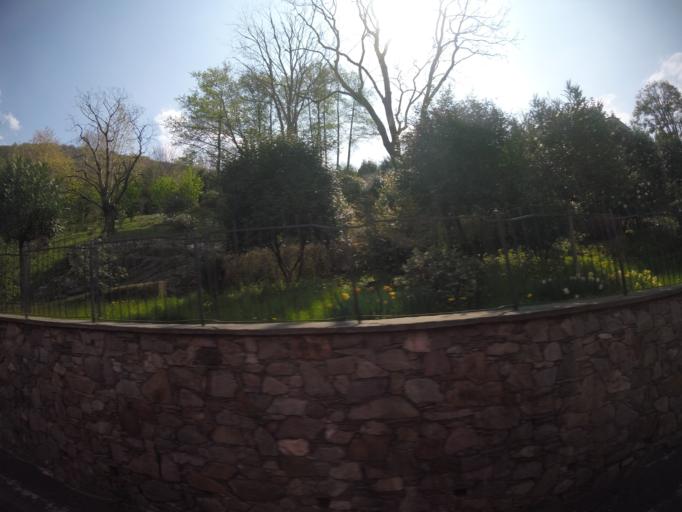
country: IT
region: Piedmont
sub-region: Provincia di Novara
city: Pettenasco
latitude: 45.8329
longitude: 8.3978
